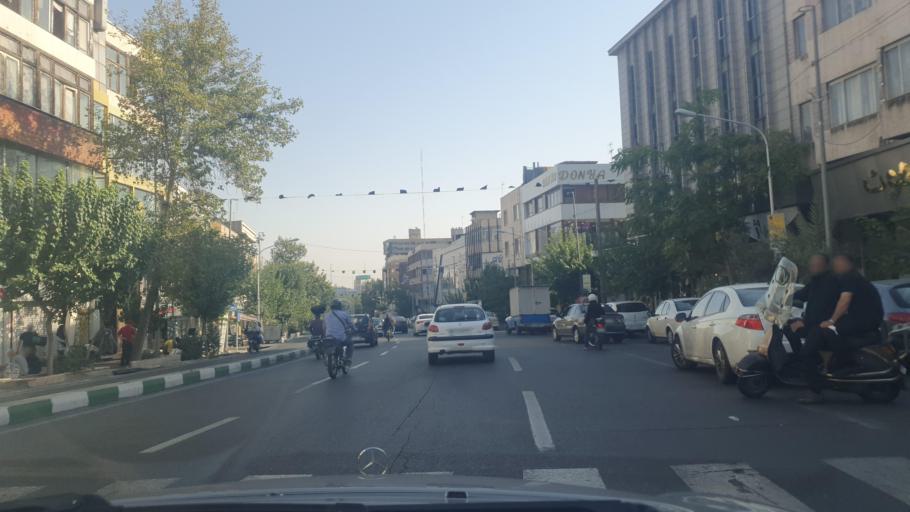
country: IR
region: Tehran
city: Tehran
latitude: 35.7147
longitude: 51.4259
